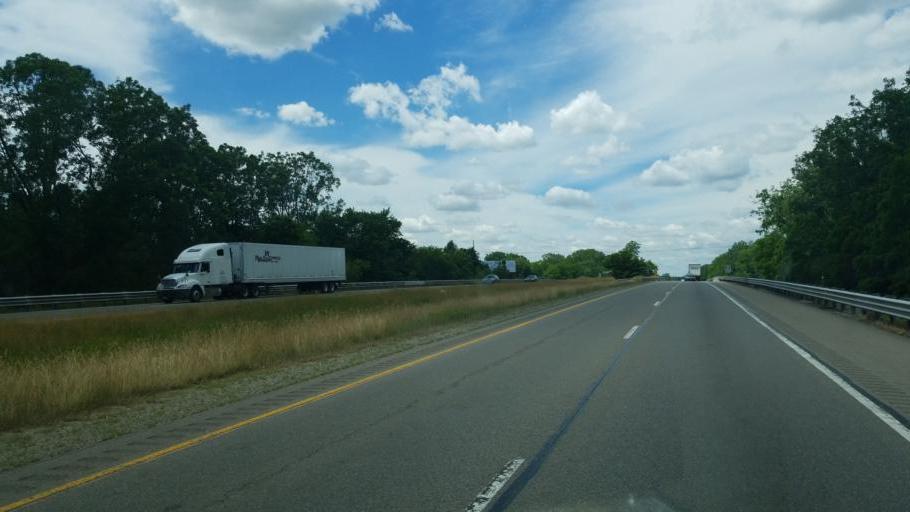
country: US
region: Michigan
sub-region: Ingham County
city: Holt
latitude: 42.6608
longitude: -84.5616
